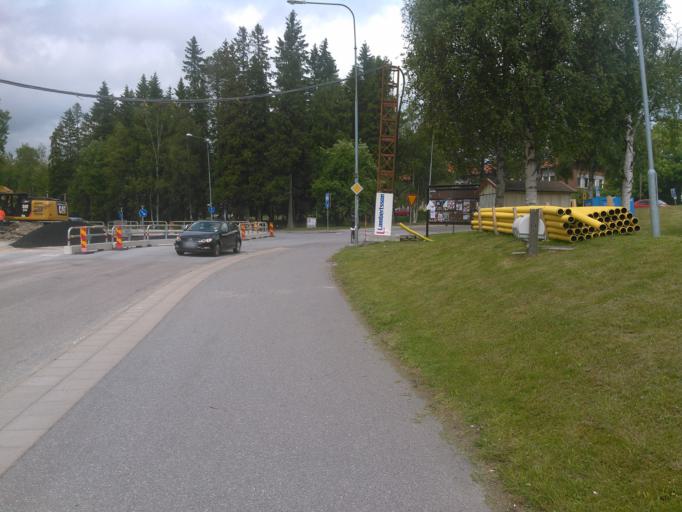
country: SE
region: Vaesterbotten
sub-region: Umea Kommun
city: Umea
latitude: 63.8260
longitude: 20.2945
